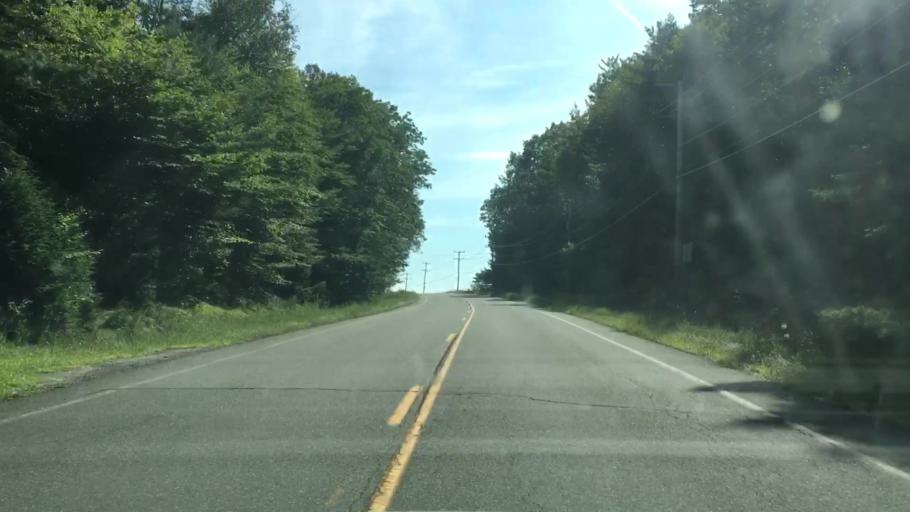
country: US
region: Maine
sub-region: Penobscot County
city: Lincoln
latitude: 45.4019
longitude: -68.5075
